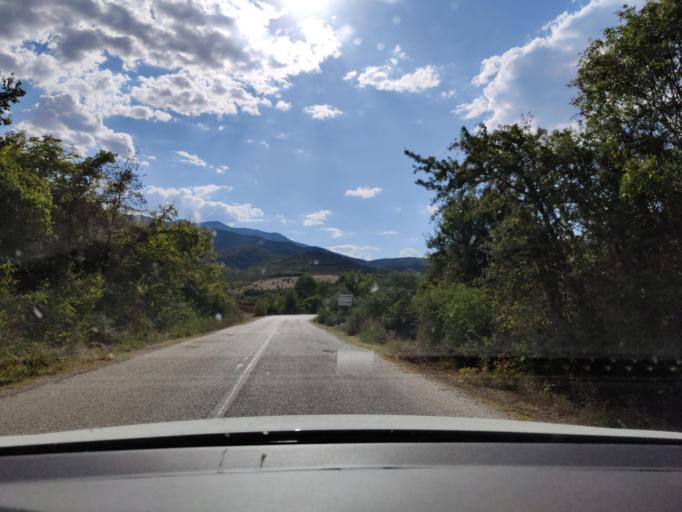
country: GR
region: Central Macedonia
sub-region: Nomos Serron
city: Chrysochorafa
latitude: 41.1476
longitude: 23.2101
